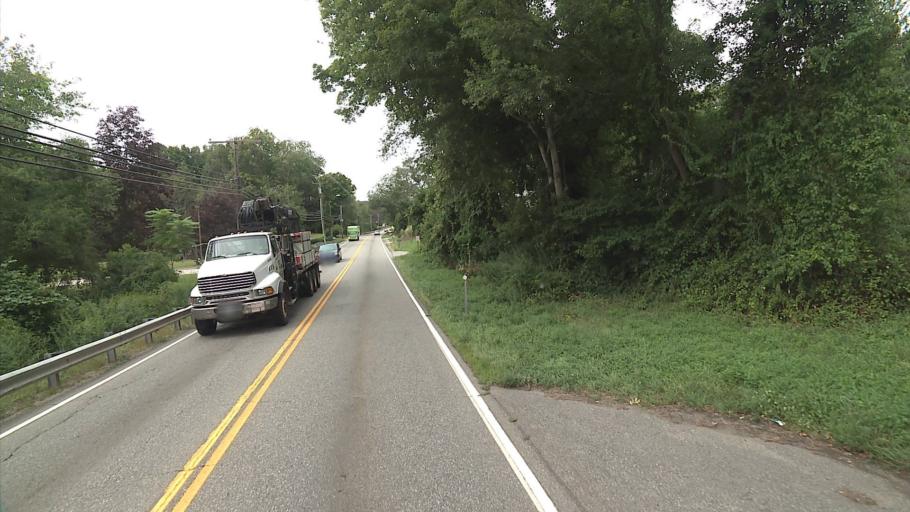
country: US
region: Connecticut
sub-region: New London County
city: Oxoboxo River
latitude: 41.4009
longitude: -72.1767
